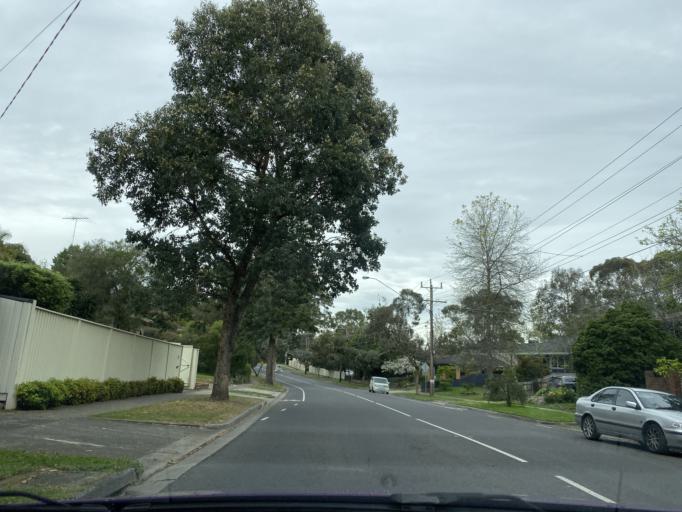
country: AU
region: Victoria
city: Saint Helena
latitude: -37.7005
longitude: 145.1289
